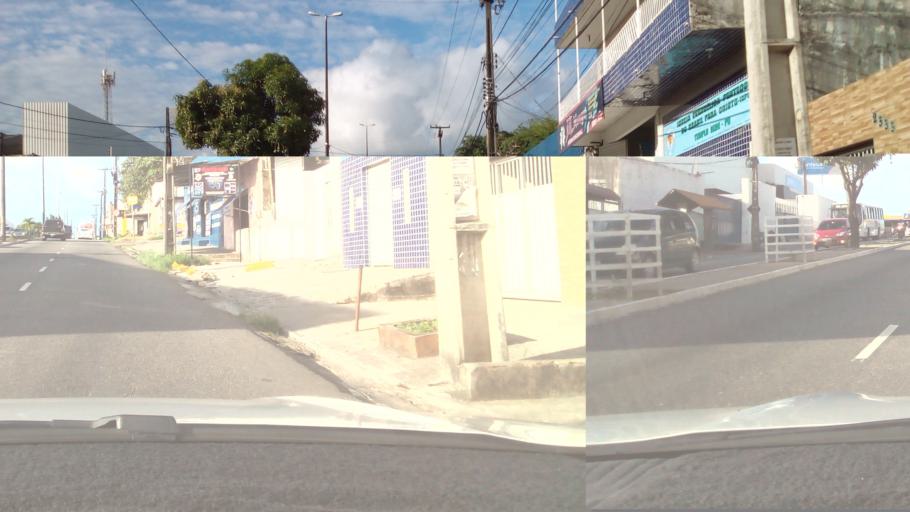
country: BR
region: Paraiba
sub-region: Bayeux
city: Bayeux
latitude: -7.1520
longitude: -34.8944
